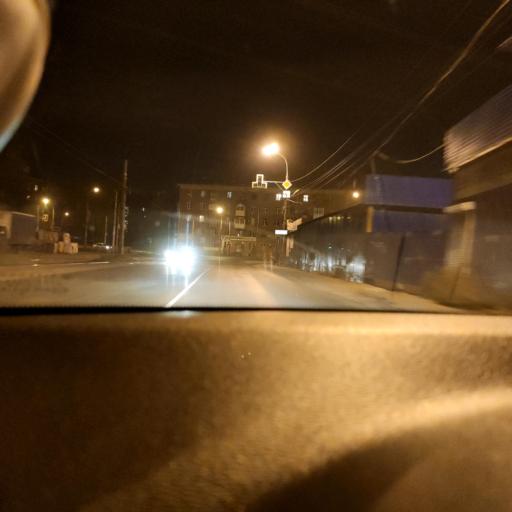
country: RU
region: Samara
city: Petra-Dubrava
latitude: 53.2266
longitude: 50.2813
